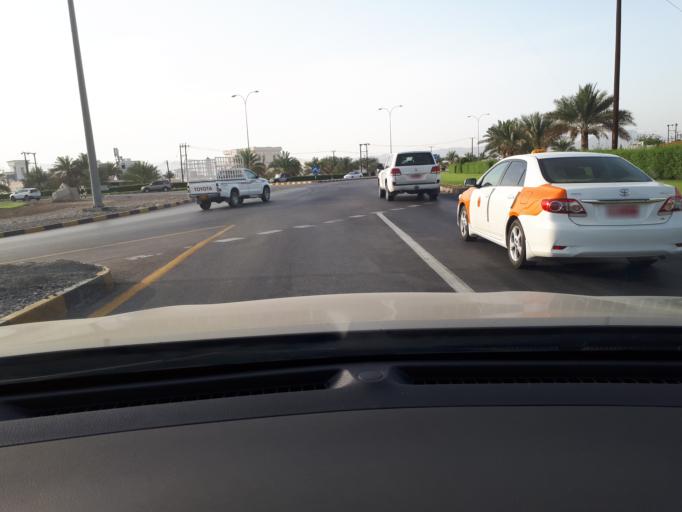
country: OM
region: Muhafazat Masqat
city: Bawshar
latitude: 23.4670
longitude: 58.4935
